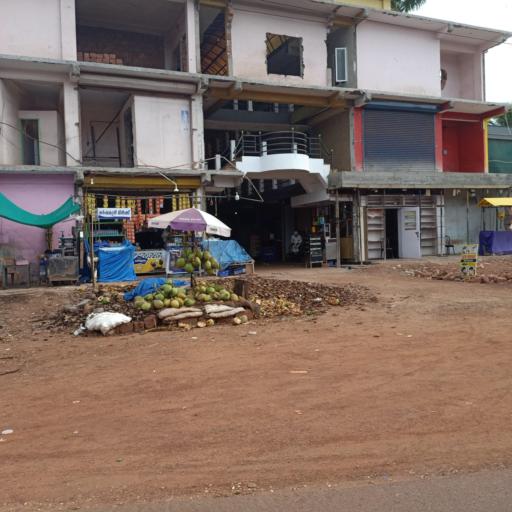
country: IN
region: Kerala
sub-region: Kasaragod District
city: Kasaragod
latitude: 12.5091
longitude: 75.0542
